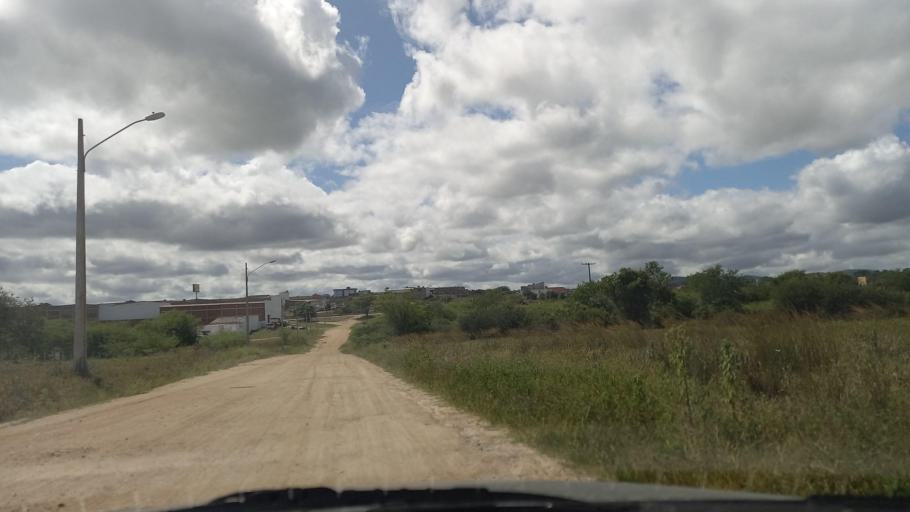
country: BR
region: Pernambuco
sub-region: Caruaru
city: Caruaru
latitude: -8.2323
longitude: -35.9814
